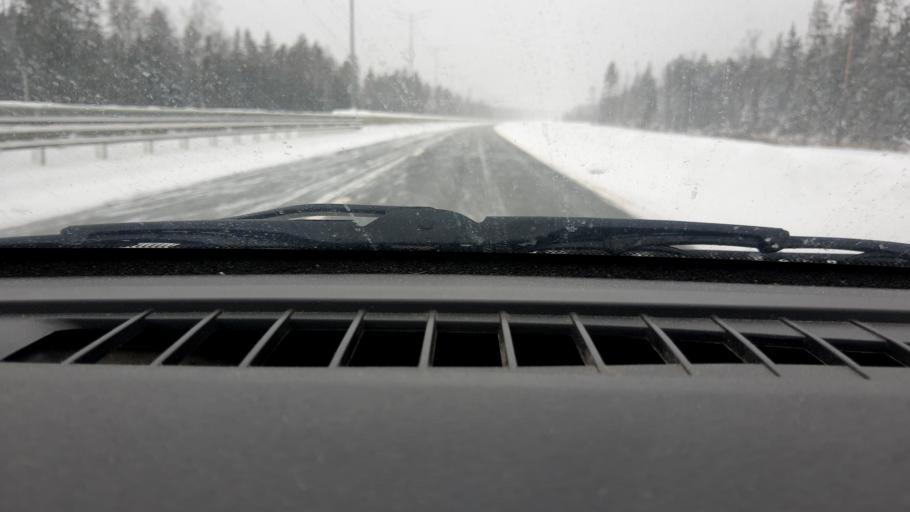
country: RU
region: Moskovskaya
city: Yamkino
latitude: 55.9526
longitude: 38.3883
